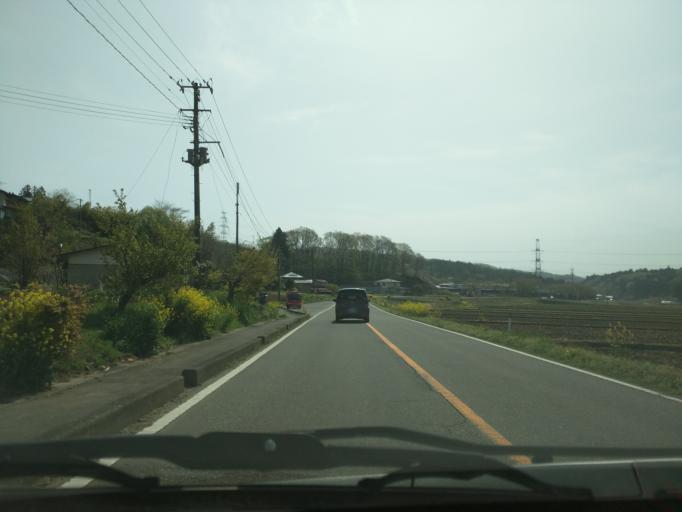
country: JP
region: Fukushima
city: Nihommatsu
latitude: 37.6010
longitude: 140.3949
